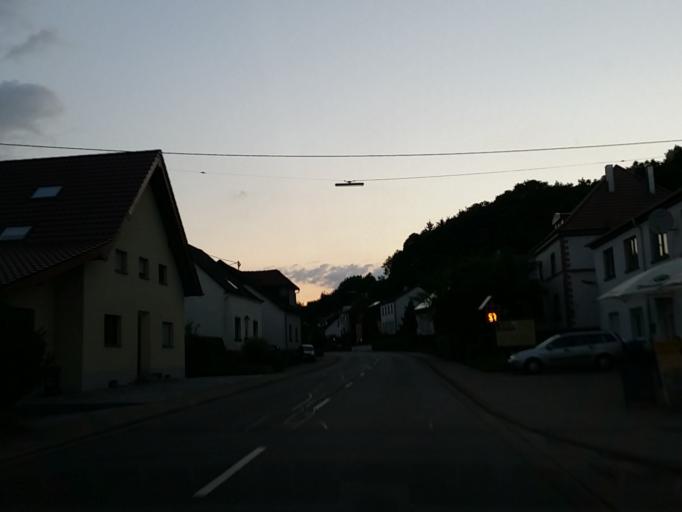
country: DE
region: Saarland
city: Schmelz
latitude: 49.4918
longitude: 6.8451
